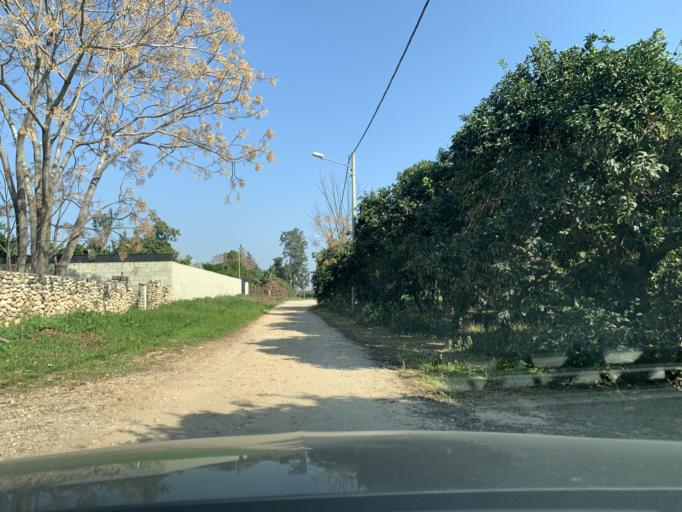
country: IL
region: Central District
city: Hod HaSharon
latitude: 32.1487
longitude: 34.9035
